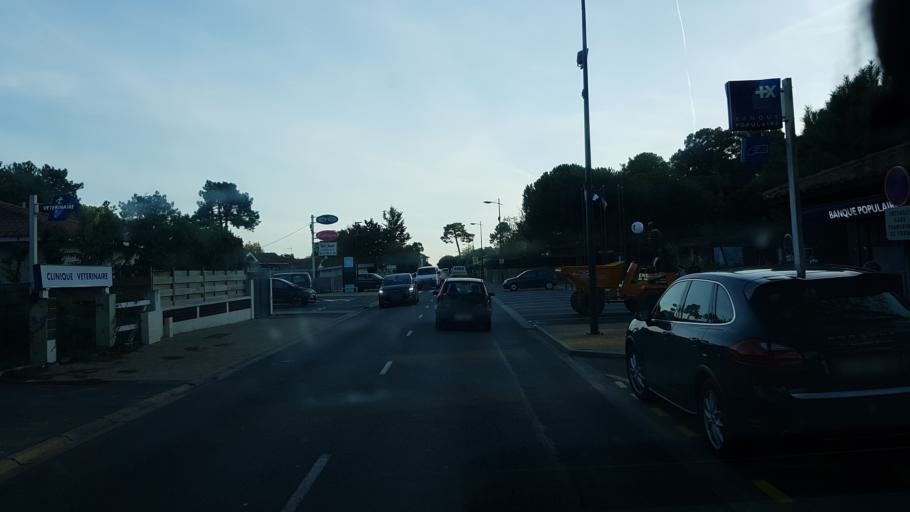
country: FR
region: Aquitaine
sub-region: Departement de la Gironde
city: Ares
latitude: 44.7474
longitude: -1.1811
